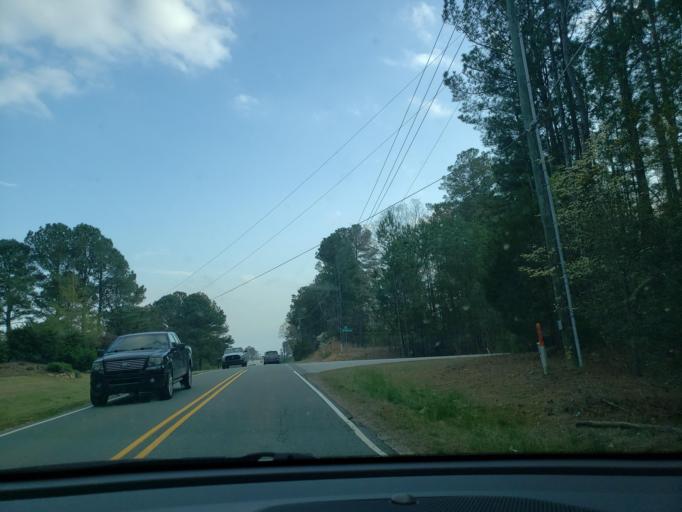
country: US
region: North Carolina
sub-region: Wake County
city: Green Level
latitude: 35.7526
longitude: -78.8944
